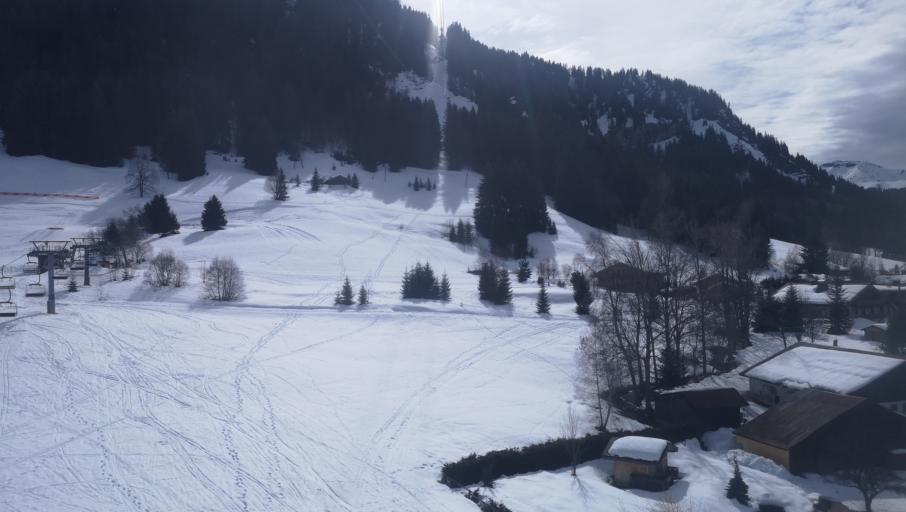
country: FR
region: Rhone-Alpes
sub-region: Departement de la Haute-Savoie
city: Megeve
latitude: 45.8468
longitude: 6.6146
